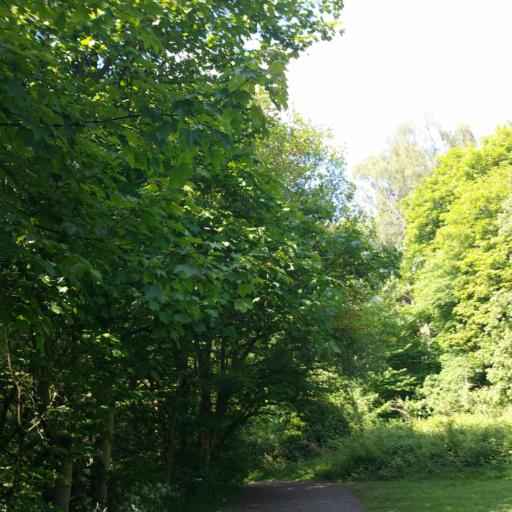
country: GB
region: Scotland
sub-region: East Dunbartonshire
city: Milngavie
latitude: 55.9485
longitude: -4.3215
